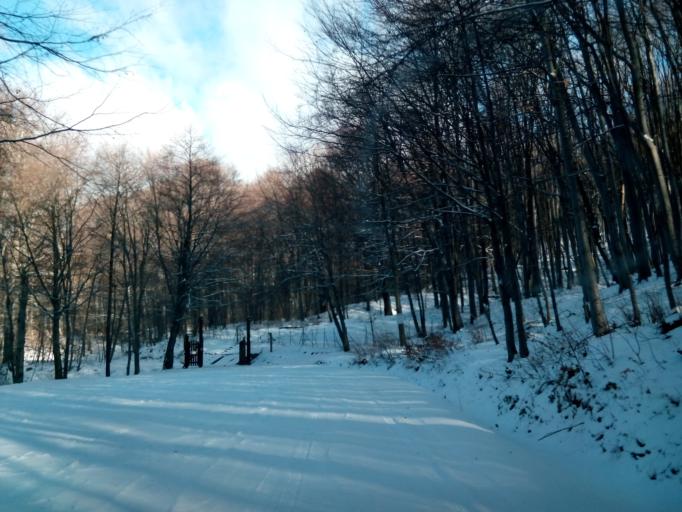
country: HU
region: Borsod-Abauj-Zemplen
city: Gonc
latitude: 48.5744
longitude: 21.4384
